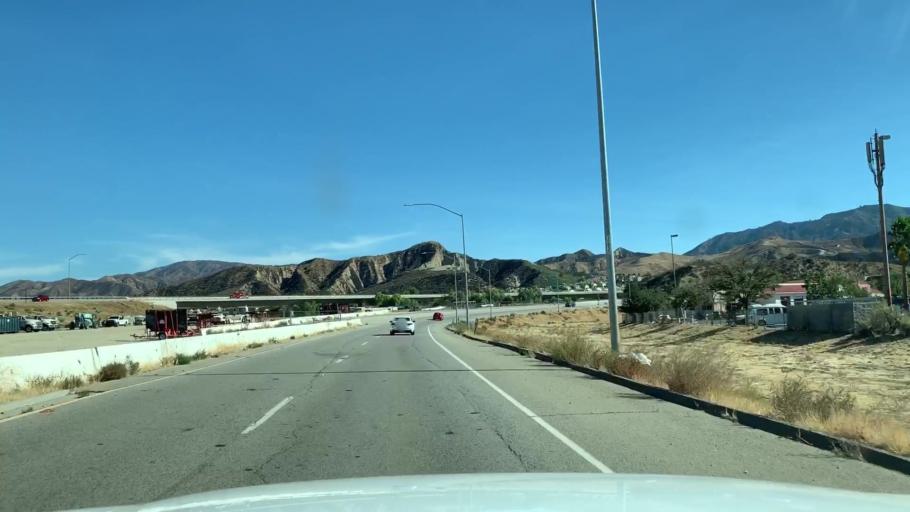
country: US
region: California
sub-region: Los Angeles County
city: Santa Clarita
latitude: 34.4050
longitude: -118.4598
